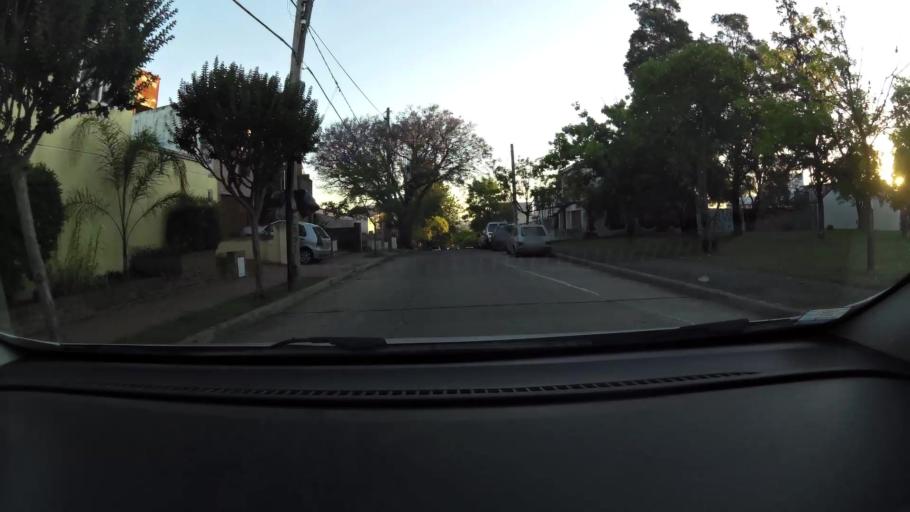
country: AR
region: Cordoba
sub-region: Departamento de Capital
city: Cordoba
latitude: -31.3796
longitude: -64.2161
